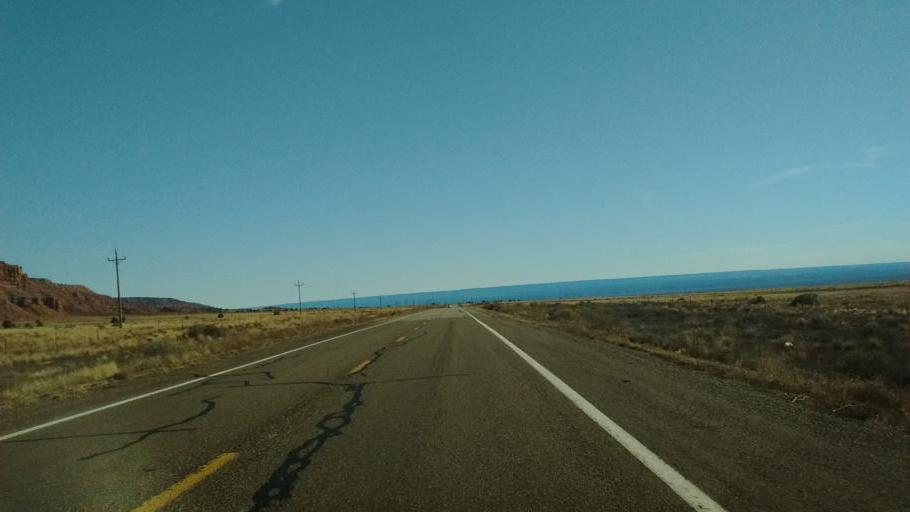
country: US
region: Arizona
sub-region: Mohave County
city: Colorado City
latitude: 36.8670
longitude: -112.8417
